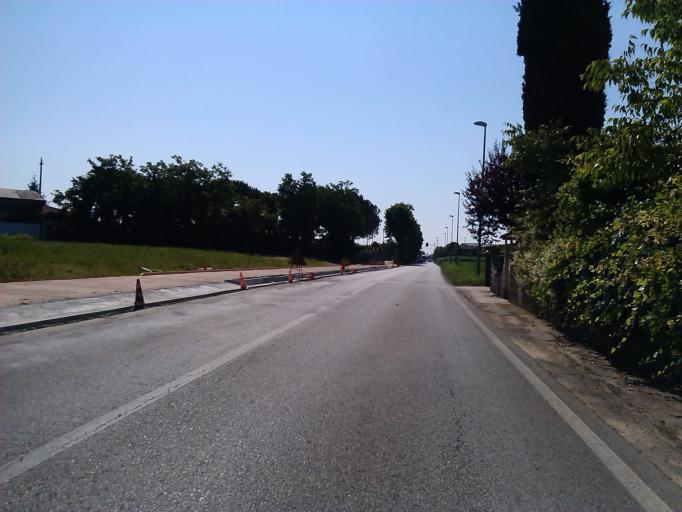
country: IT
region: Veneto
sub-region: Provincia di Vicenza
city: Cassola
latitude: 45.7530
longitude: 11.7884
